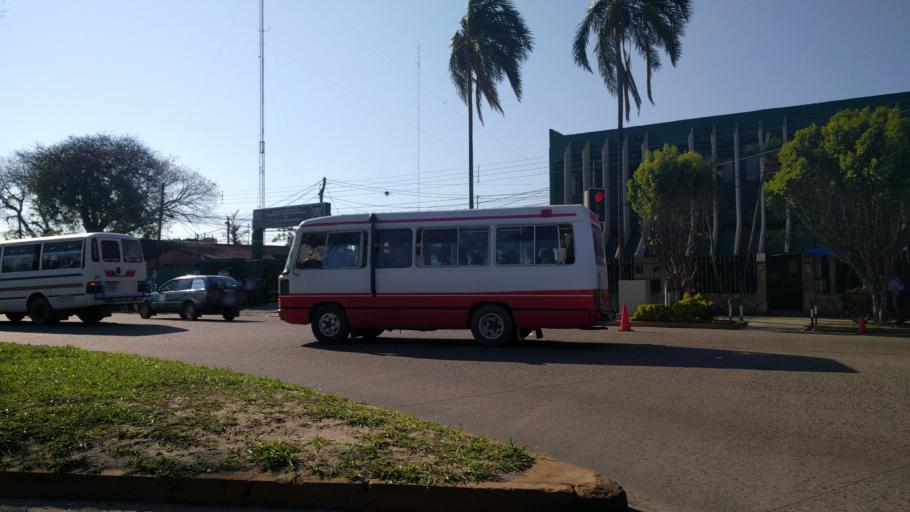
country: BO
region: Santa Cruz
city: Santa Cruz de la Sierra
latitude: -17.8128
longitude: -63.1824
